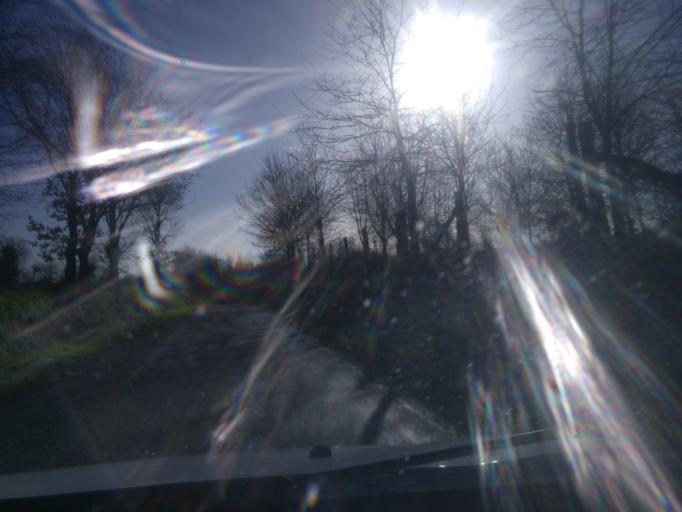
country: FR
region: Brittany
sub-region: Departement d'Ille-et-Vilaine
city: Pleine-Fougeres
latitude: 48.5319
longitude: -1.5367
